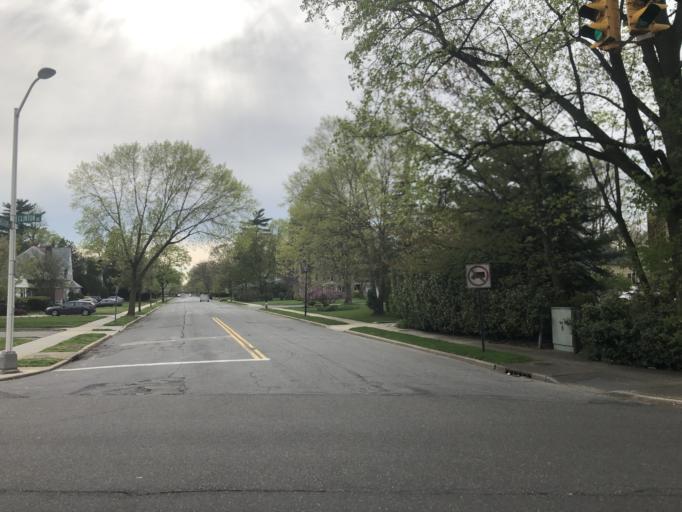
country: US
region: New York
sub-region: Nassau County
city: Hempstead
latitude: 40.7198
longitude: -73.6208
